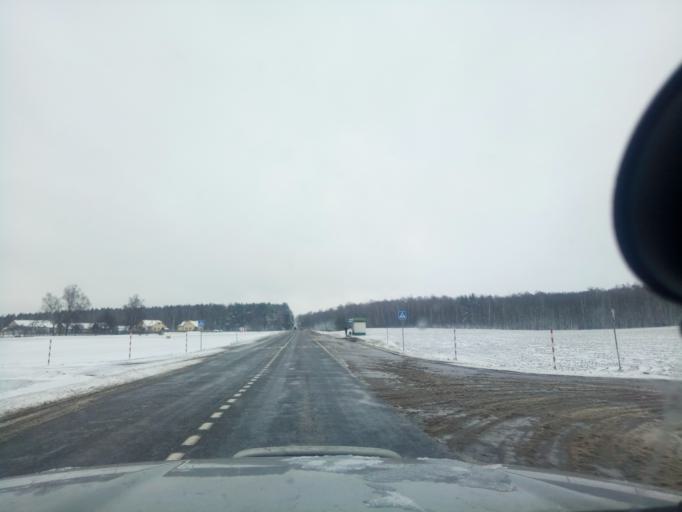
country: BY
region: Minsk
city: Kapyl'
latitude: 53.1236
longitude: 27.0739
